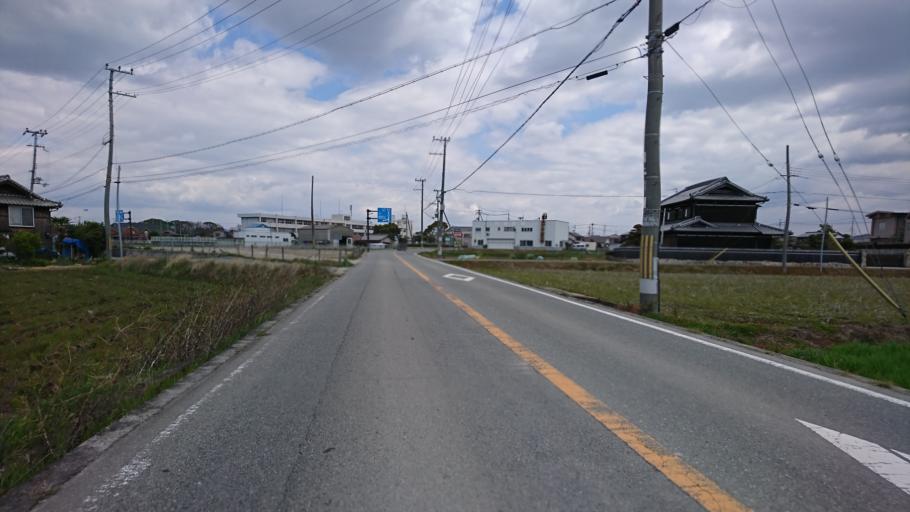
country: JP
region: Hyogo
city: Miki
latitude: 34.7520
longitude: 134.9410
